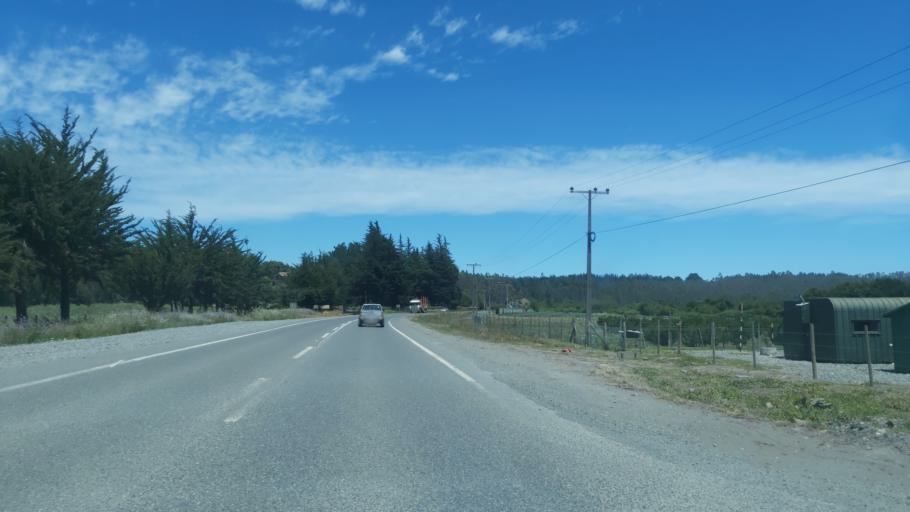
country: CL
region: Maule
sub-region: Provincia de Talca
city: Constitucion
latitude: -35.3108
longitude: -72.3816
